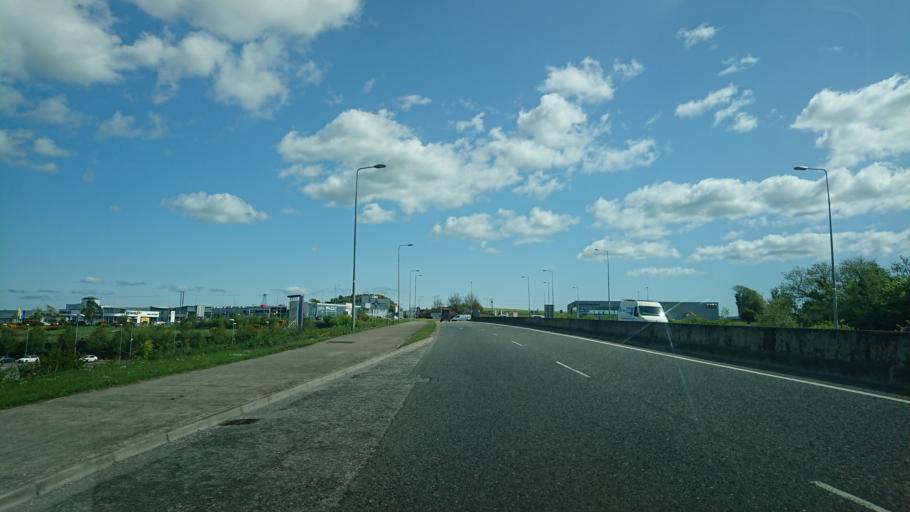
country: IE
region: Munster
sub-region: Waterford
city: Waterford
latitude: 52.2440
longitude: -7.1701
